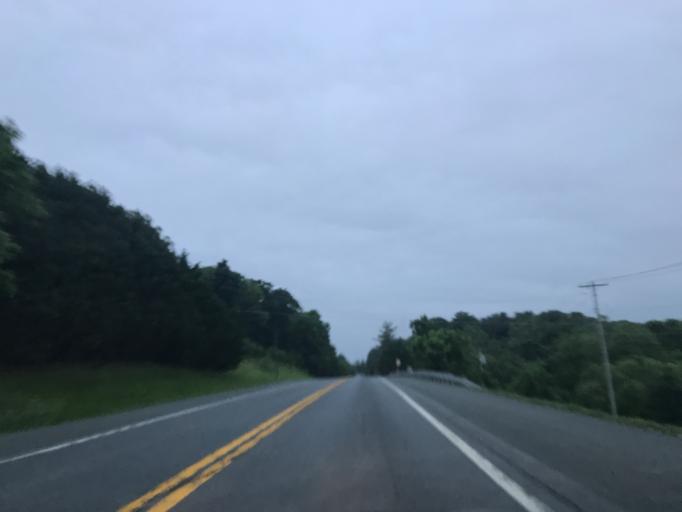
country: US
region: Maryland
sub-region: Frederick County
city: Linganore
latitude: 39.4417
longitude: -77.2507
